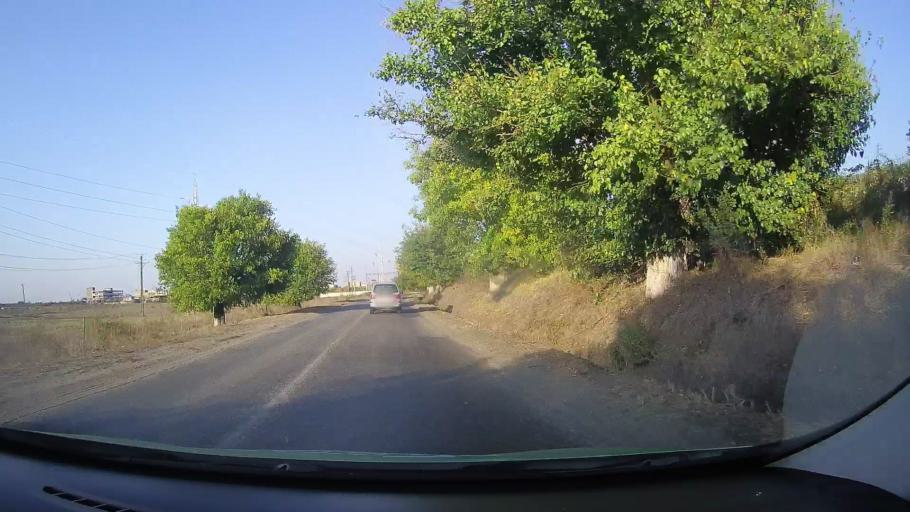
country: RO
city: Masca
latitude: 46.3140
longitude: 21.6791
